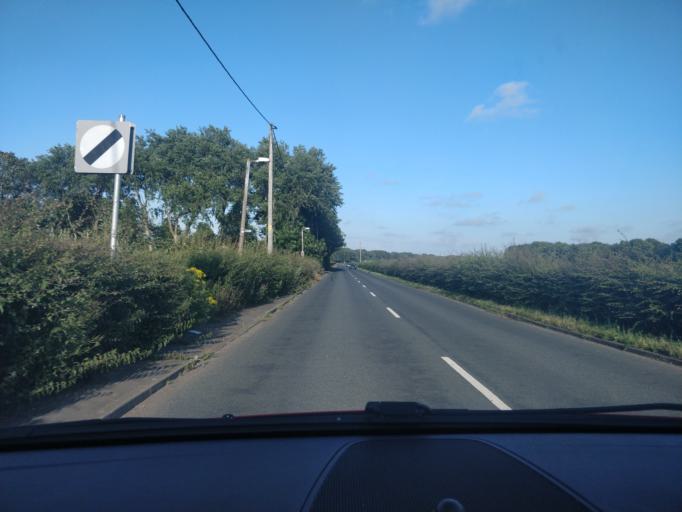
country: GB
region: England
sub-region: Lancashire
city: Tarleton
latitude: 53.6401
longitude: -2.8419
